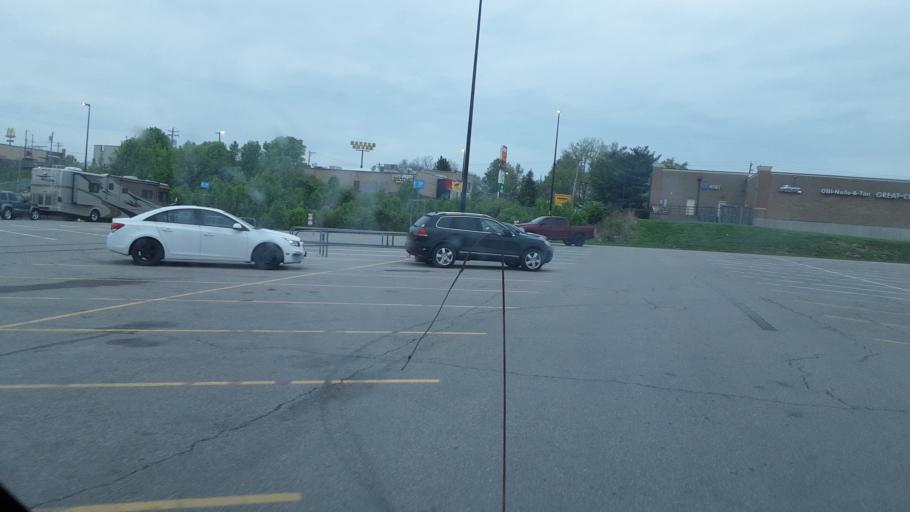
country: US
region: Kentucky
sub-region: Grant County
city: Dry Ridge
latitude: 38.6802
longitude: -84.5970
